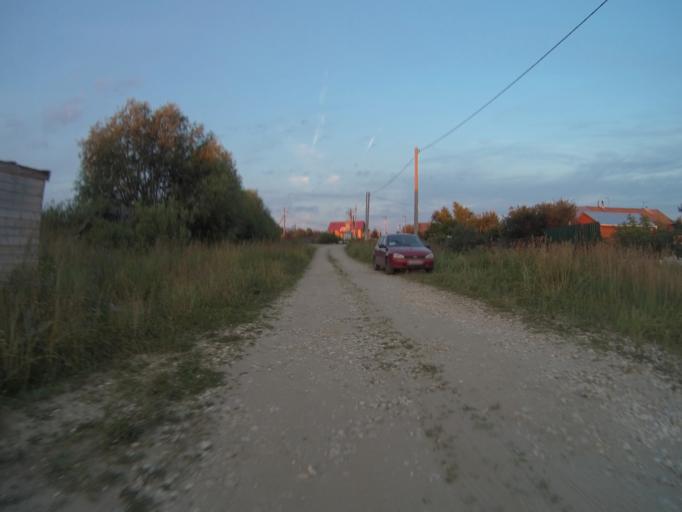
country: RU
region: Vladimir
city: Kommunar
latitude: 56.0823
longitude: 40.4924
